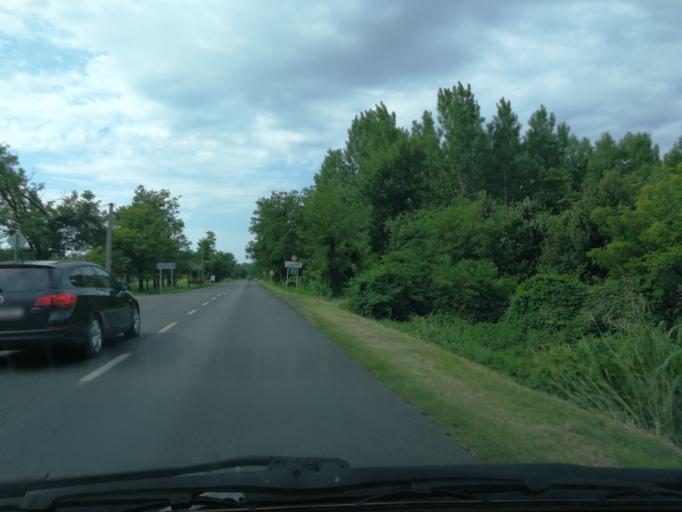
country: HU
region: Bacs-Kiskun
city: Ersekcsanad
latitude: 46.2444
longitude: 18.9781
